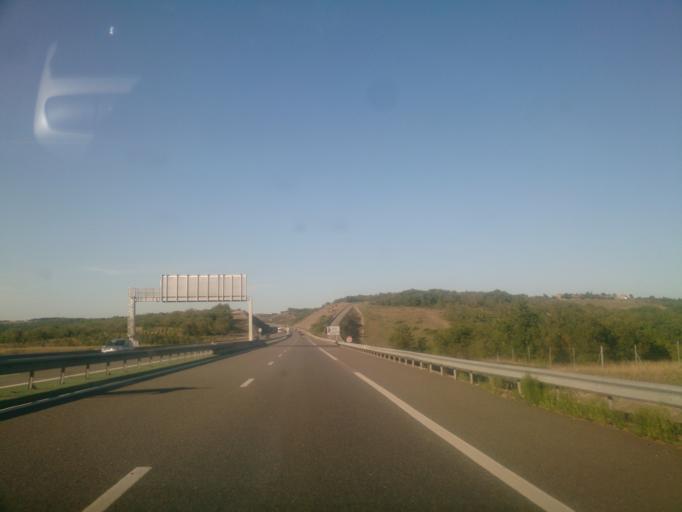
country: FR
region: Midi-Pyrenees
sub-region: Departement du Lot
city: Cahors
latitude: 44.5087
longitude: 1.5002
